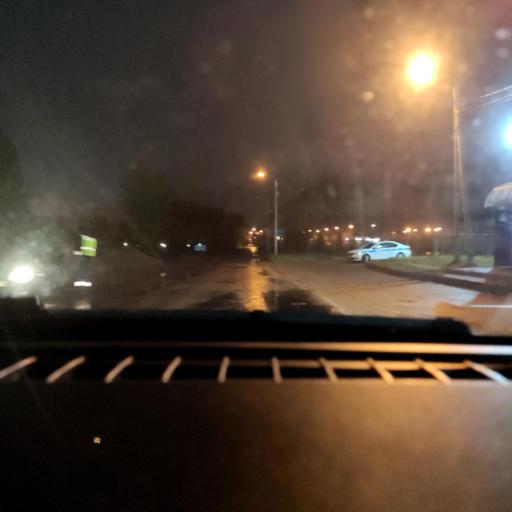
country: RU
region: Voronezj
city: Somovo
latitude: 51.6779
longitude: 39.2916
